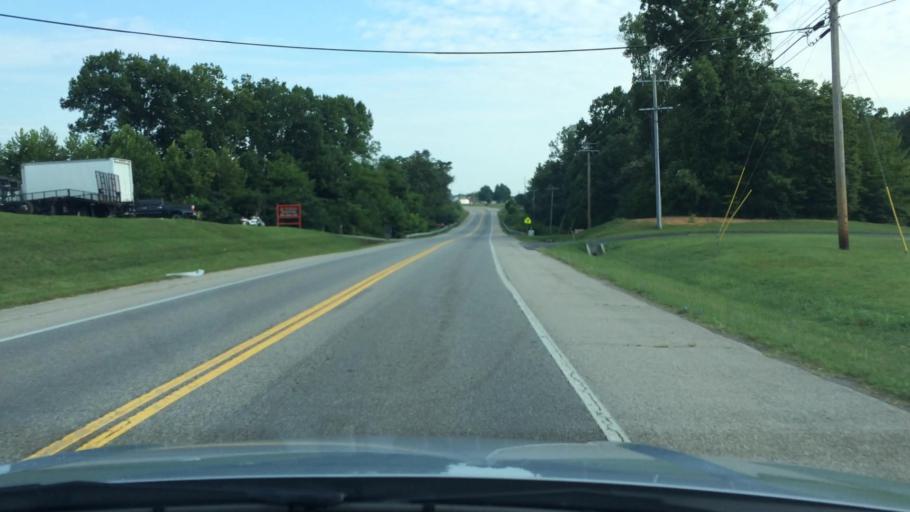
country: US
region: Tennessee
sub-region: Blount County
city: Maryville
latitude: 35.7338
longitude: -84.0349
